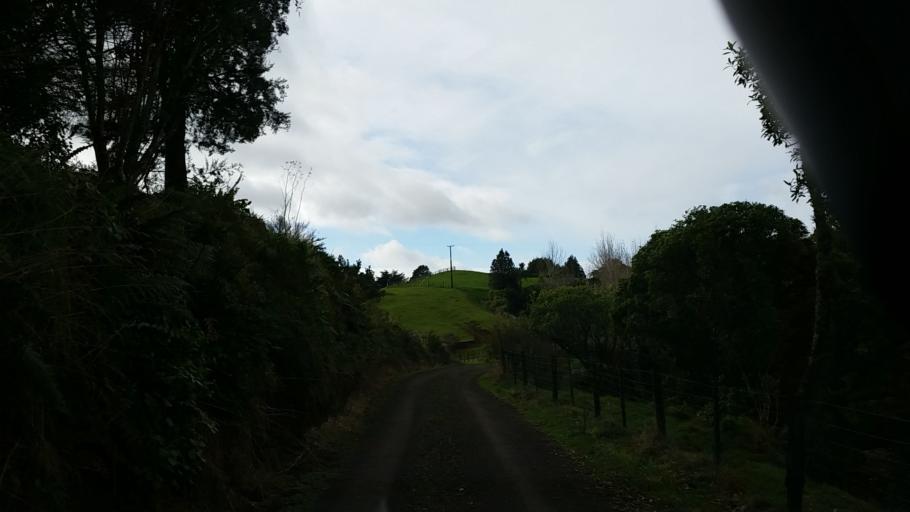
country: NZ
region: Taranaki
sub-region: New Plymouth District
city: Waitara
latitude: -39.0687
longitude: 174.3973
